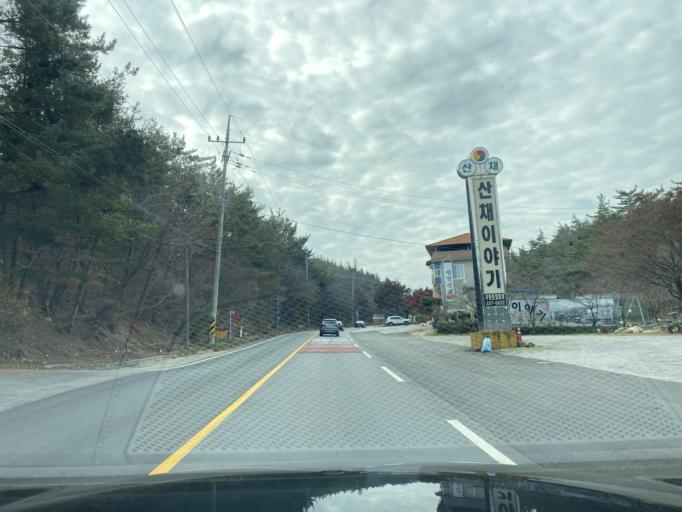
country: KR
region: Chungcheongnam-do
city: Hongsung
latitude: 36.6715
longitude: 126.6417
